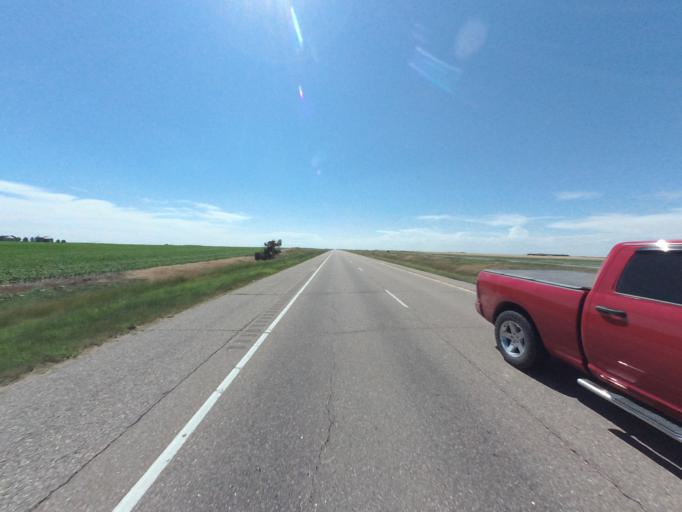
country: US
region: Colorado
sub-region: Kit Carson County
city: Burlington
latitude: 39.2940
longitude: -102.3144
